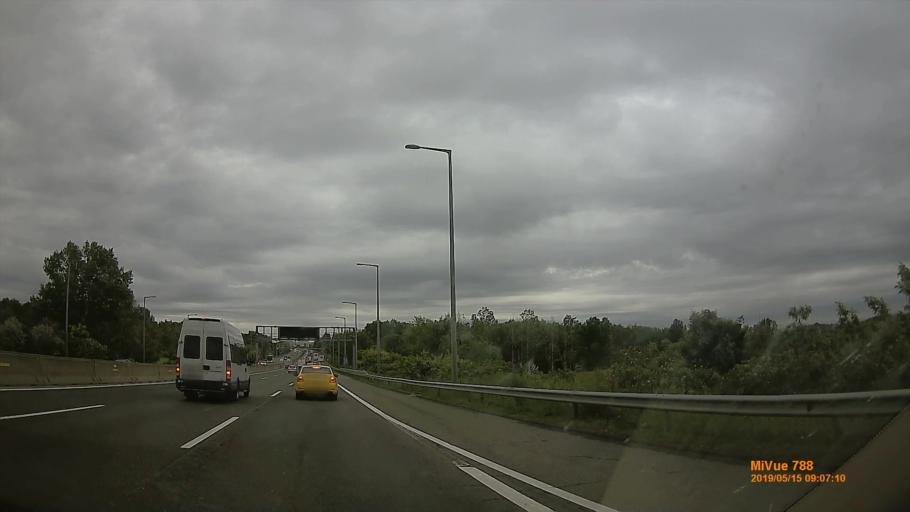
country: HU
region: Pest
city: Budaors
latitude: 47.4592
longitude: 18.9931
